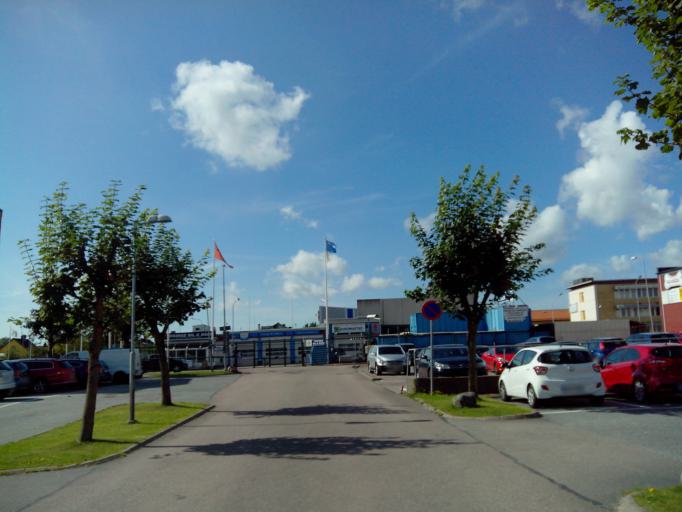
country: SE
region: Vaestra Goetaland
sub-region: Goteborg
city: Goeteborg
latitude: 57.7253
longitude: 11.9478
